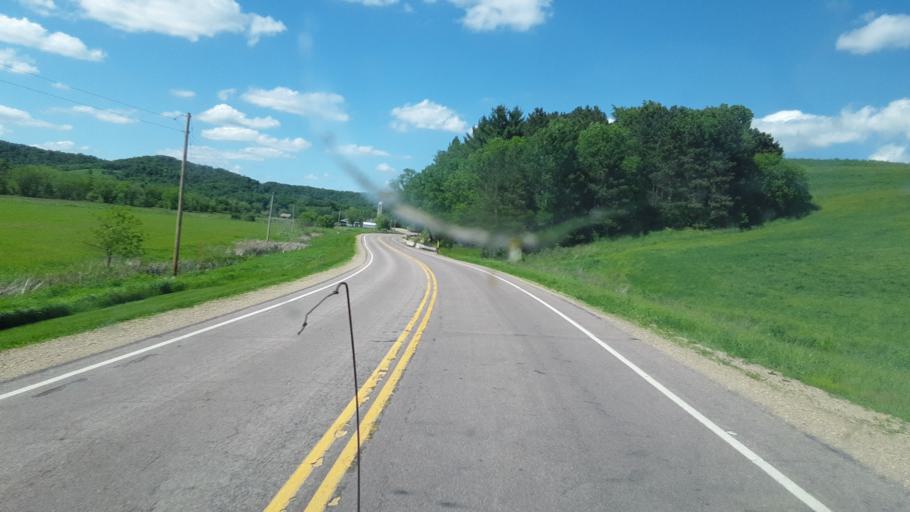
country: US
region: Wisconsin
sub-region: Richland County
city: Richland Center
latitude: 43.3628
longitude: -90.2656
